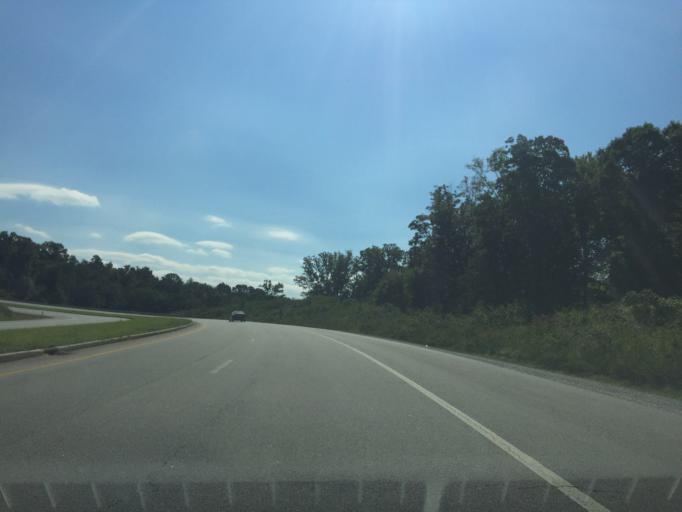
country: US
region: Tennessee
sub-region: Hamilton County
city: Harrison
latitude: 35.0737
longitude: -85.1258
